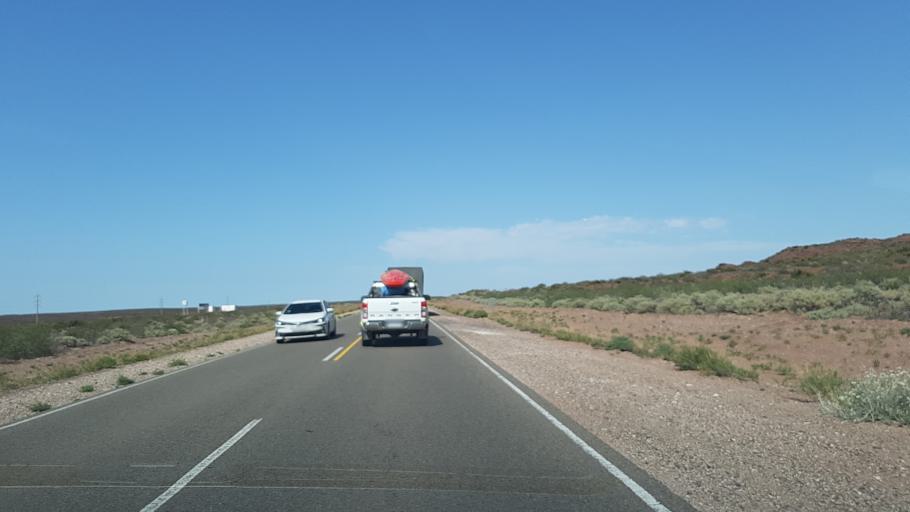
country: AR
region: Neuquen
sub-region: Departamento de Picun Leufu
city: Picun Leufu
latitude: -39.2900
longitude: -68.8802
